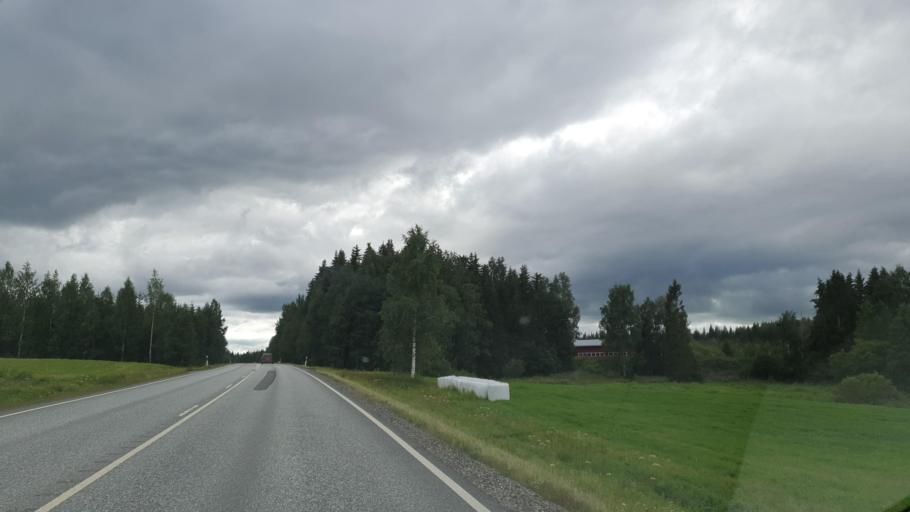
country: FI
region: Northern Savo
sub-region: Ylae-Savo
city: Sonkajaervi
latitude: 63.7549
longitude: 27.3909
